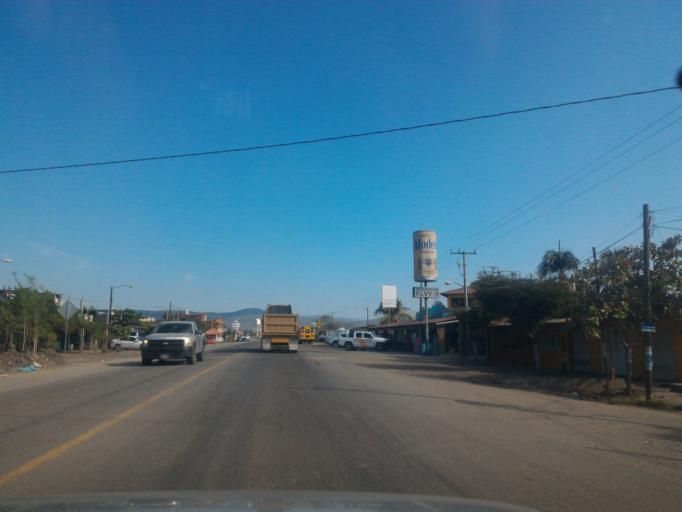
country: MX
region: Michoacan
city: Coahuayana Viejo
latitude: 18.7514
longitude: -103.7243
